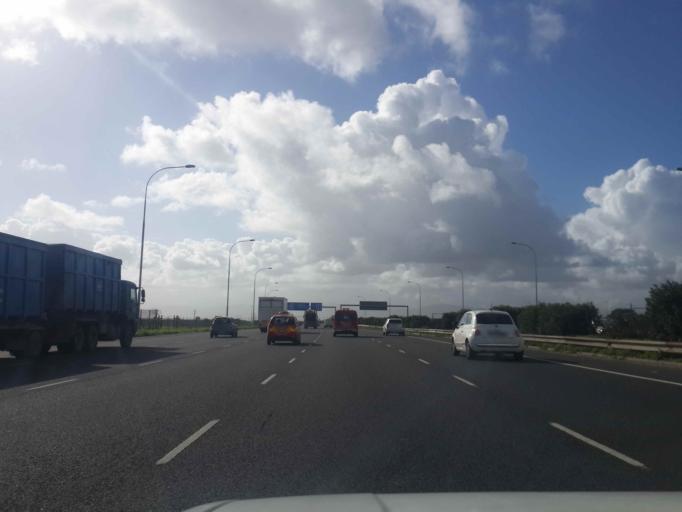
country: ZA
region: Western Cape
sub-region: City of Cape Town
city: Rosebank
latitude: -33.9138
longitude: 18.4946
